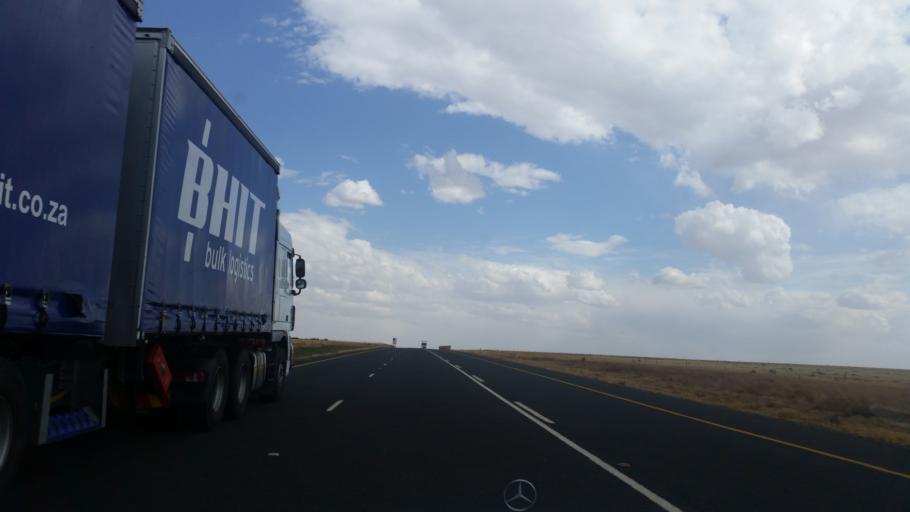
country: ZA
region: Orange Free State
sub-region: Xhariep District Municipality
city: Trompsburg
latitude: -29.7067
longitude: 25.9724
